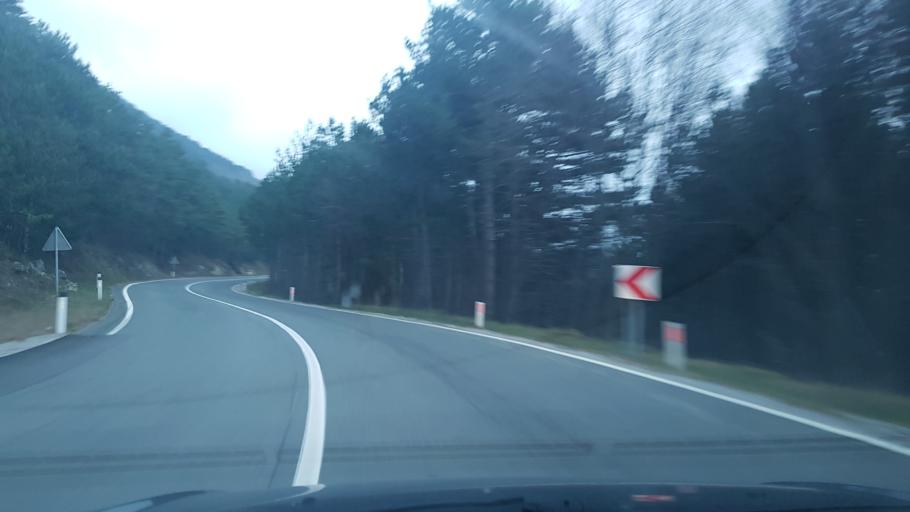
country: SI
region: Vipava
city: Vipava
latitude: 45.8801
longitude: 13.9546
